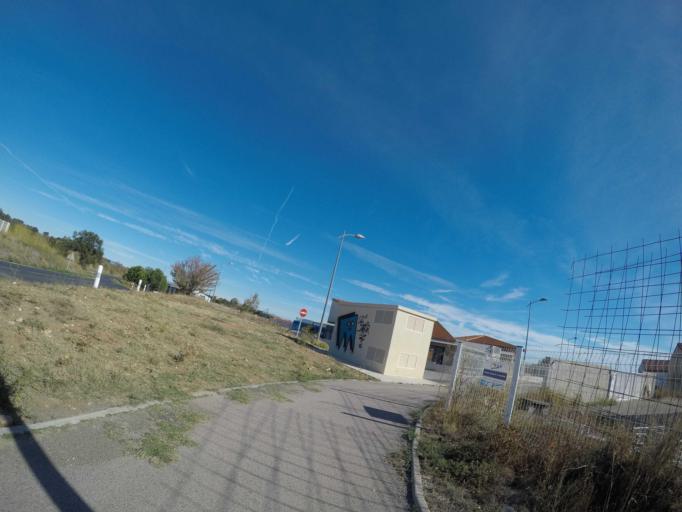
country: FR
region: Languedoc-Roussillon
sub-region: Departement des Pyrenees-Orientales
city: Trouillas
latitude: 42.6176
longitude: 2.8117
